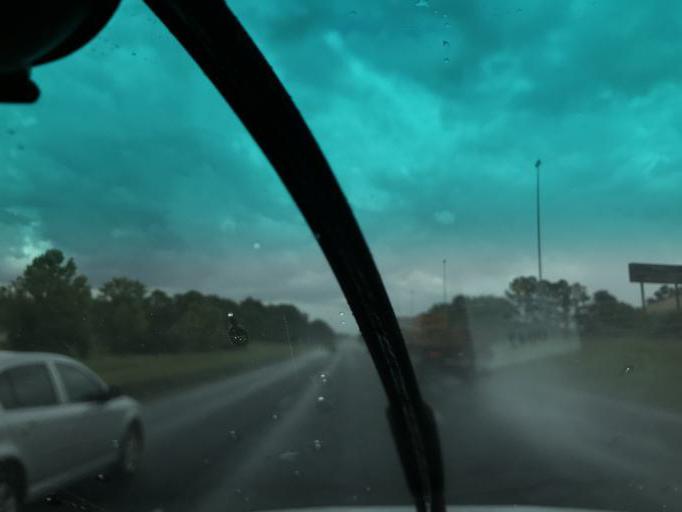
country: US
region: Alabama
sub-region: Montgomery County
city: Montgomery
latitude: 32.3622
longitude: -86.2055
